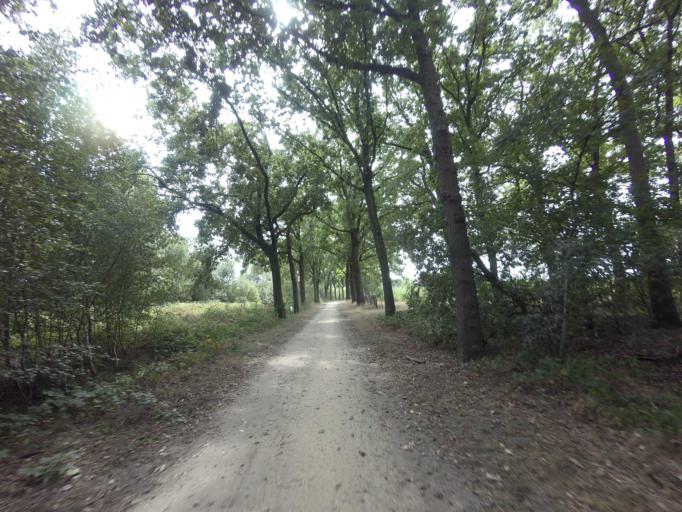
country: NL
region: North Brabant
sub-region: Gemeente Helmond
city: Helmond
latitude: 51.5153
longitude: 5.7604
